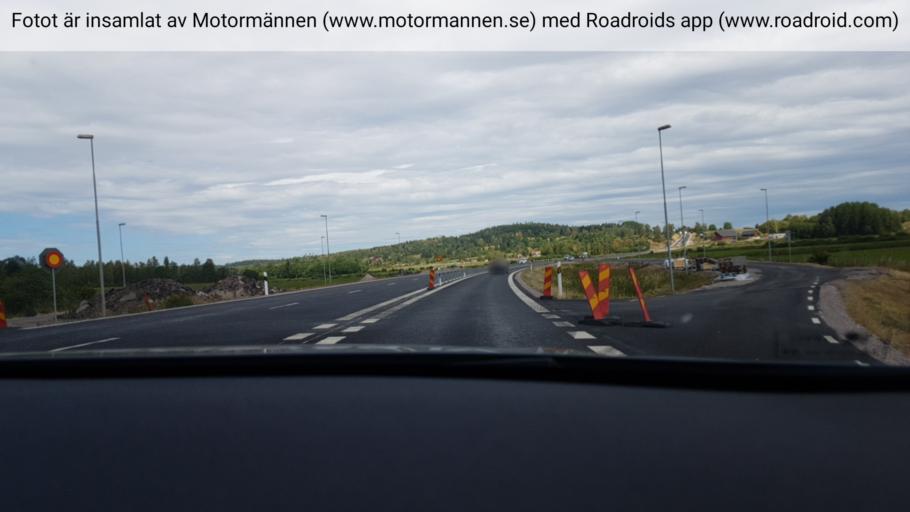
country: SE
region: Joenkoeping
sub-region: Tranas Kommun
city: Tranas
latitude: 58.0012
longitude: 14.9200
